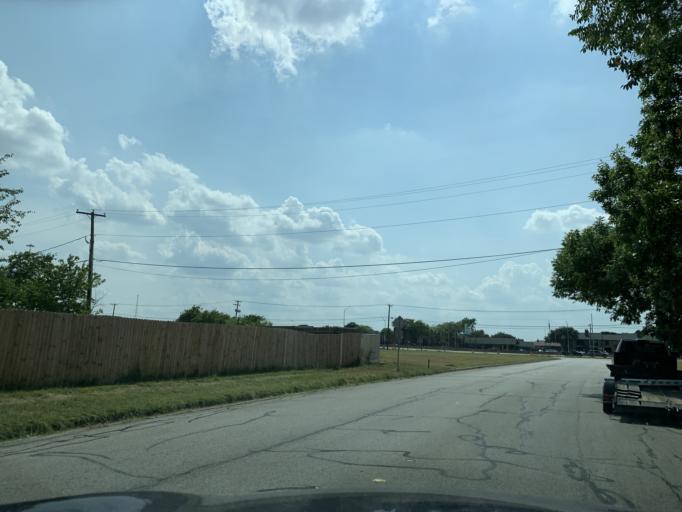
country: US
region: Texas
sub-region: Tarrant County
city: Richland Hills
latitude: 32.7723
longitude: -97.2108
